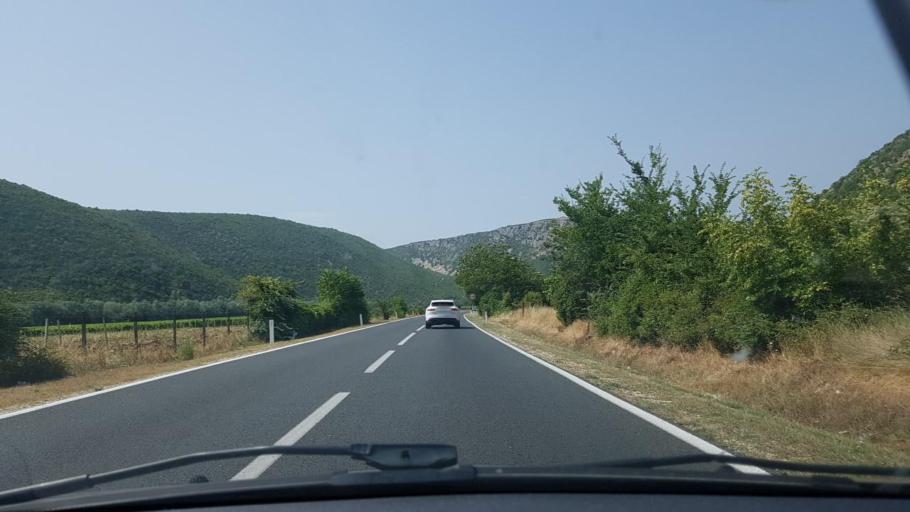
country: BA
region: Federation of Bosnia and Herzegovina
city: Citluk
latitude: 43.1840
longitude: 17.7830
